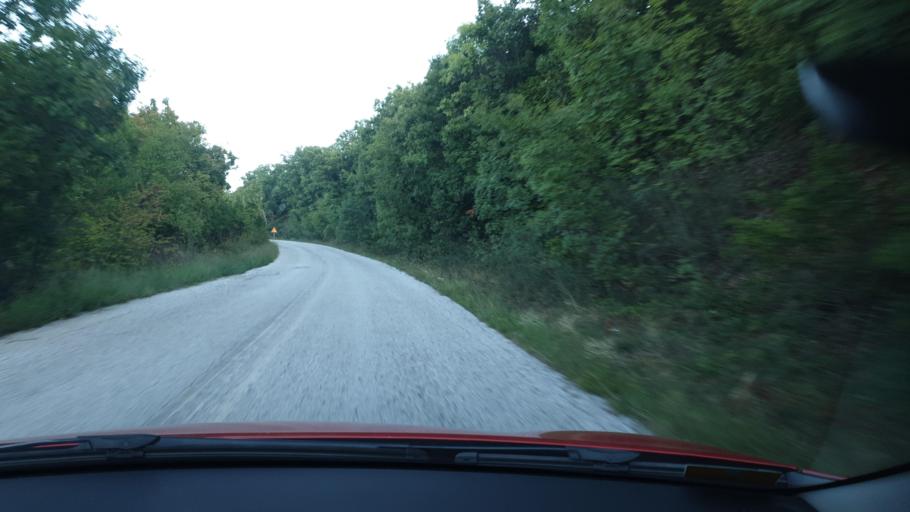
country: GR
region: Central Macedonia
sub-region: Nomos Chalkidikis
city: Galatista
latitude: 40.5417
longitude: 23.2838
